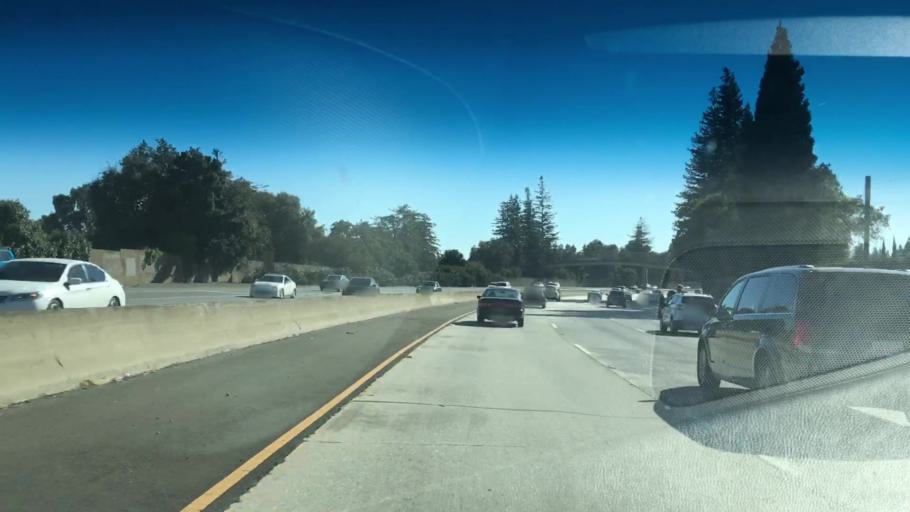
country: US
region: California
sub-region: Yolo County
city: West Sacramento
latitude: 38.5309
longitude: -121.5178
